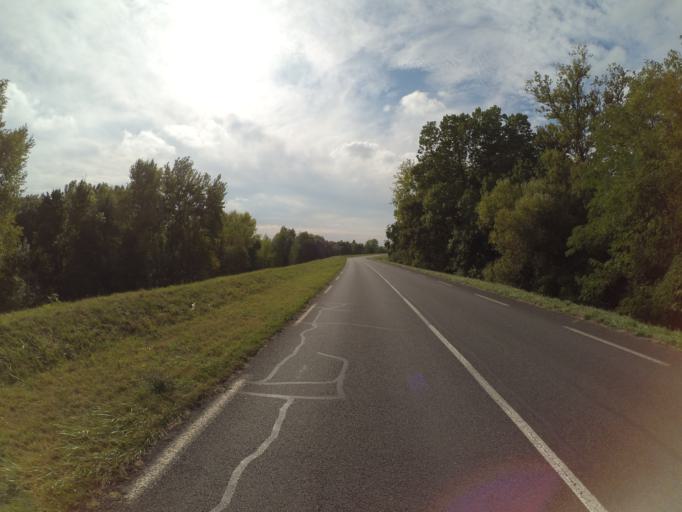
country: FR
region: Centre
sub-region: Departement d'Indre-et-Loire
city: Huismes
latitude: 47.2748
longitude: 0.3077
